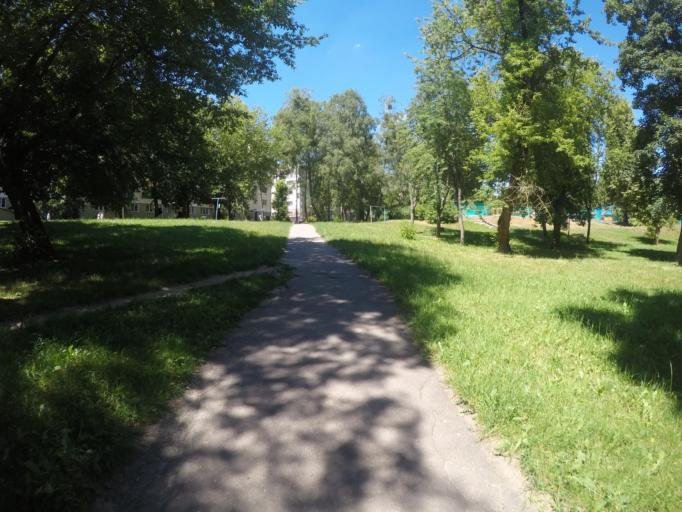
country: BY
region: Grodnenskaya
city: Hrodna
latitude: 53.6959
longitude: 23.8228
